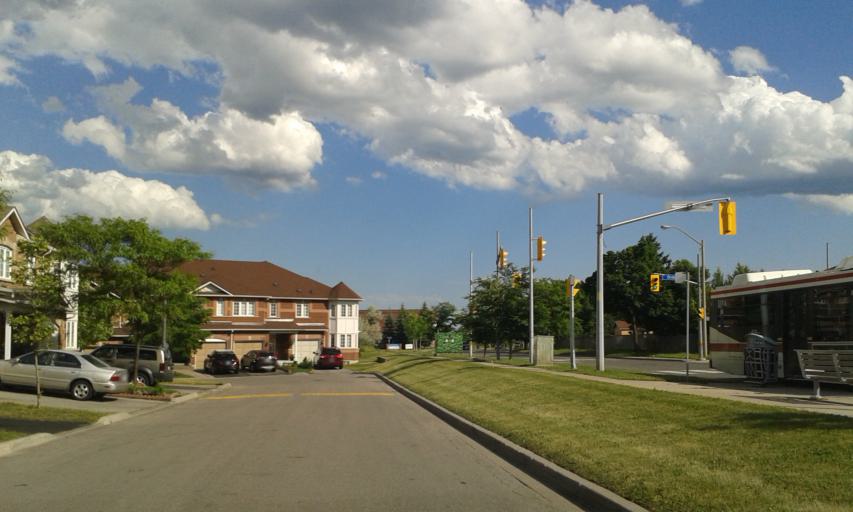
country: CA
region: Ontario
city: Scarborough
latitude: 43.8084
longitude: -79.2565
